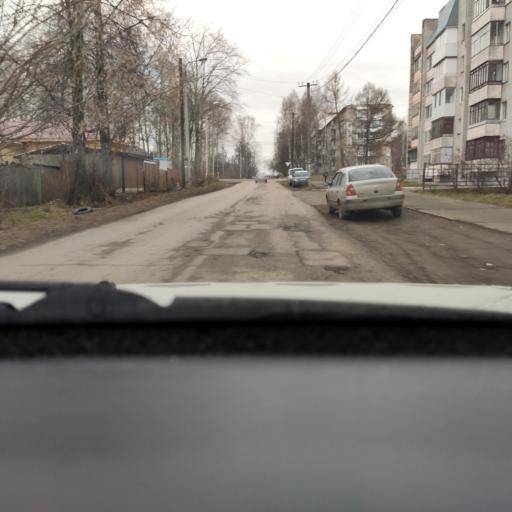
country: RU
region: Perm
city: Polazna
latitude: 58.1290
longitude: 56.3906
